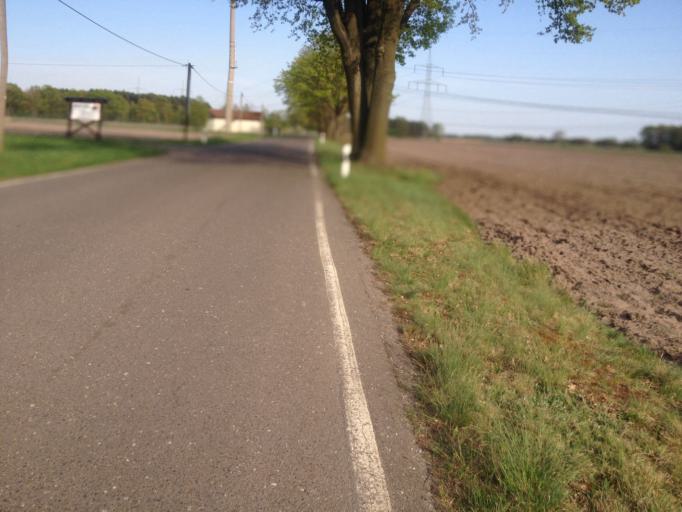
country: DE
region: Brandenburg
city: Drachhausen
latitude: 51.8756
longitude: 14.3193
